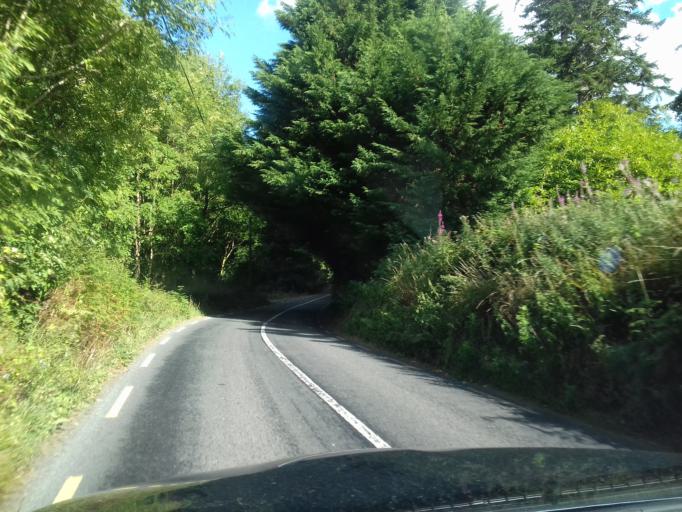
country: IE
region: Leinster
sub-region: Kilkenny
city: Thomastown
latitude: 52.5492
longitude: -7.0652
